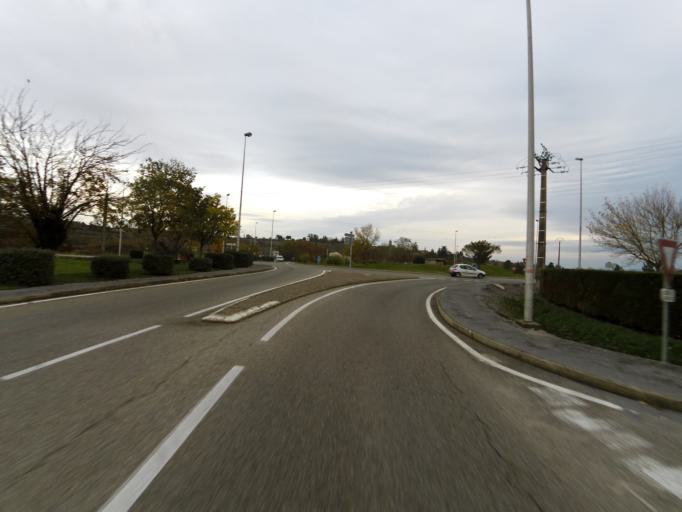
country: FR
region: Rhone-Alpes
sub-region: Departement de l'Ardeche
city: Lablachere
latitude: 44.4605
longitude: 4.2181
